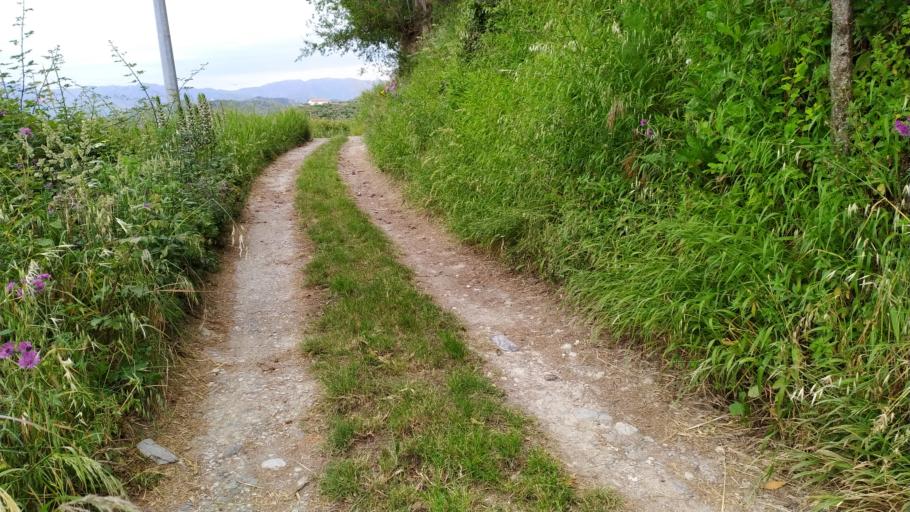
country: IT
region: Sicily
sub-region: Messina
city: Pace del Mela
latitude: 38.1627
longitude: 15.2943
